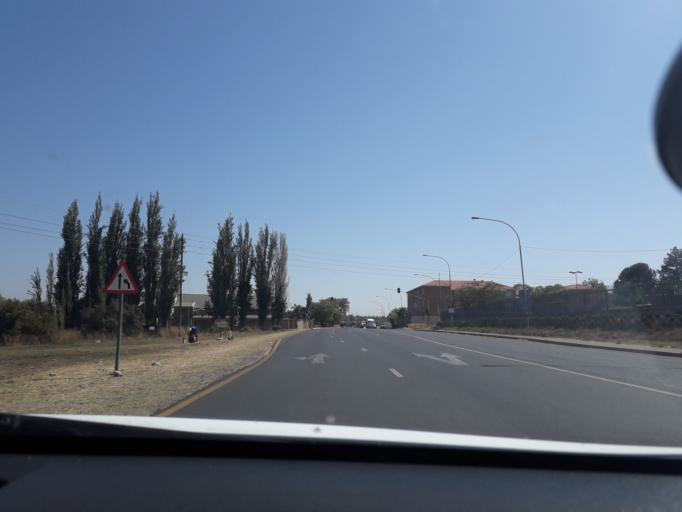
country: ZA
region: Gauteng
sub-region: City of Johannesburg Metropolitan Municipality
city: Modderfontein
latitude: -26.0961
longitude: 28.2197
